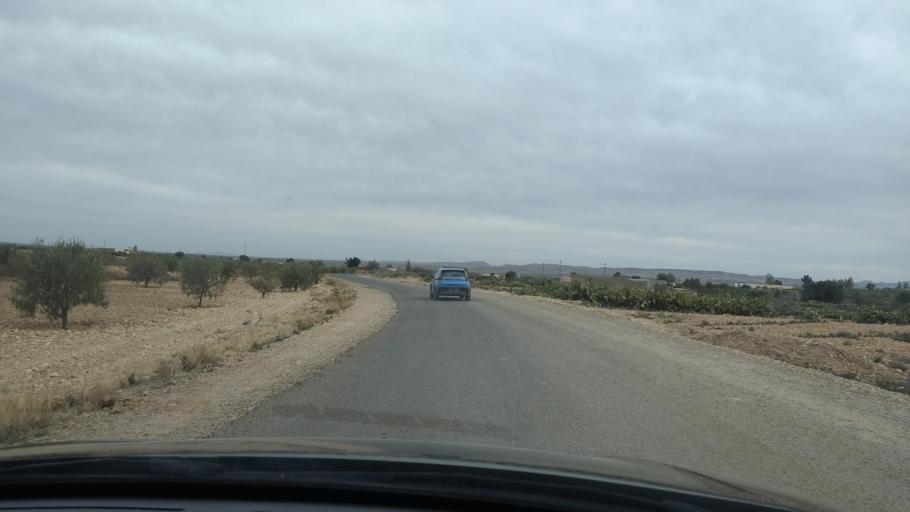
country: TN
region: Al Qasrayn
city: Kasserine
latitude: 35.2637
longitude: 8.9347
